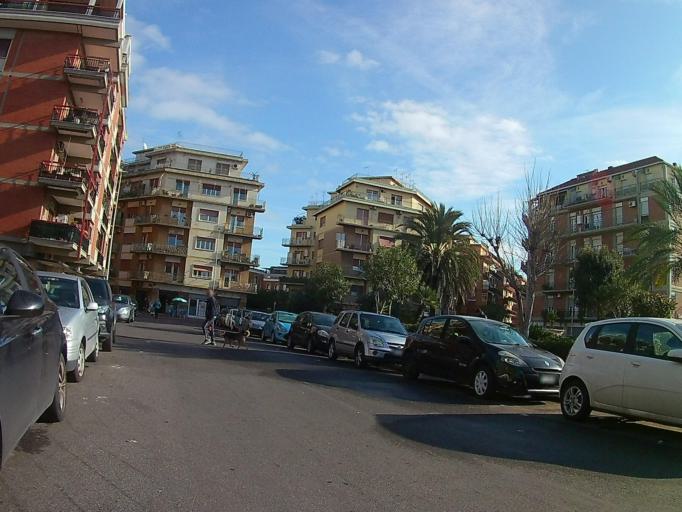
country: IT
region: Latium
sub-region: Citta metropolitana di Roma Capitale
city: Lido di Ostia
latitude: 41.7335
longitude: 12.2689
